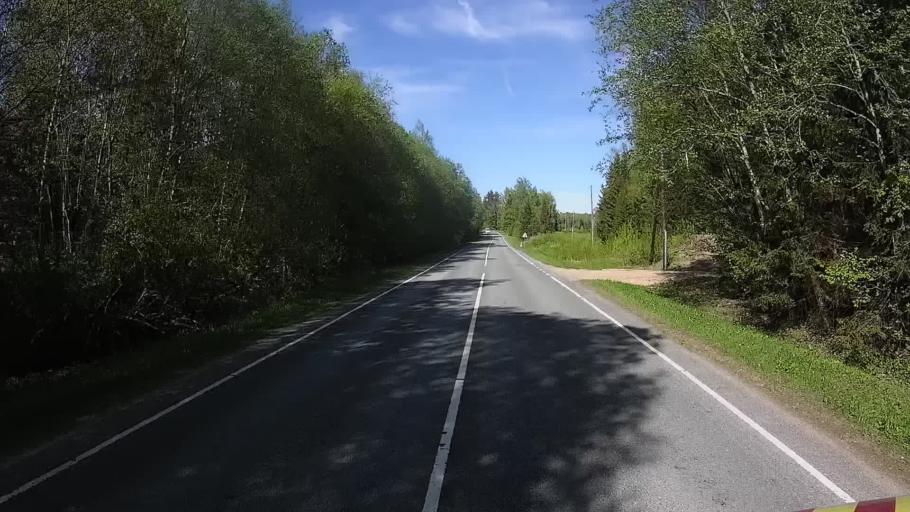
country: EE
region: Vorumaa
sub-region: Antsla vald
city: Vana-Antsla
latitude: 57.9651
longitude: 26.4580
